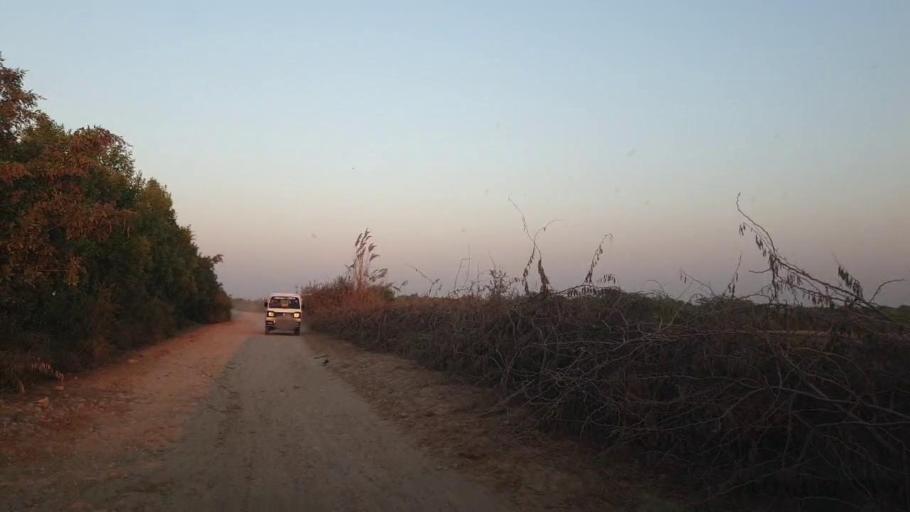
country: PK
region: Sindh
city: Mirpur Sakro
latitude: 24.4227
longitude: 67.5924
